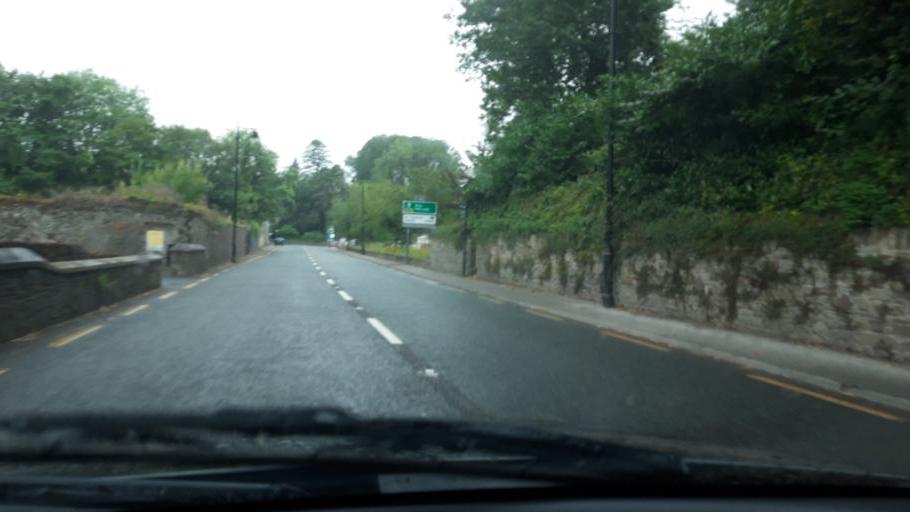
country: IE
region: Munster
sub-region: County Cork
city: Youghal
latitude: 52.1435
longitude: -7.9266
